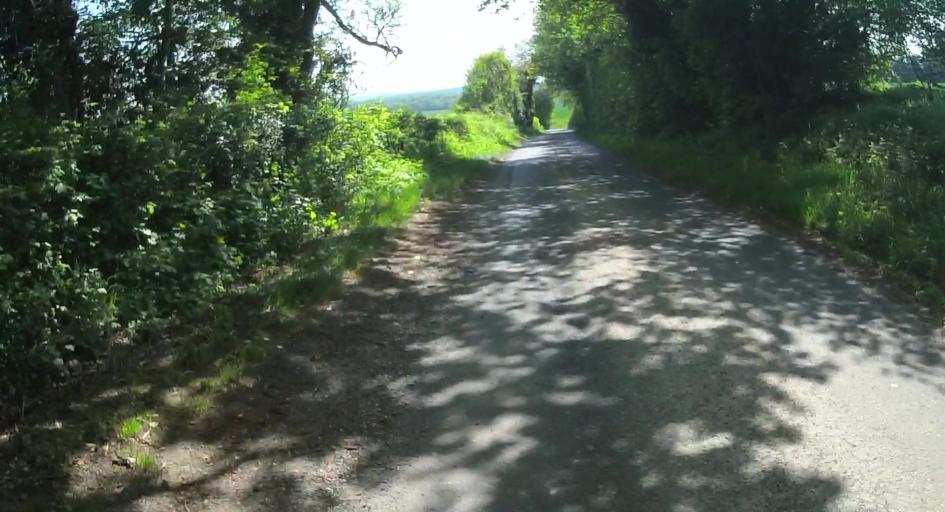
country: GB
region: England
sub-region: Hampshire
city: Four Marks
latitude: 51.1250
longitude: -1.0950
